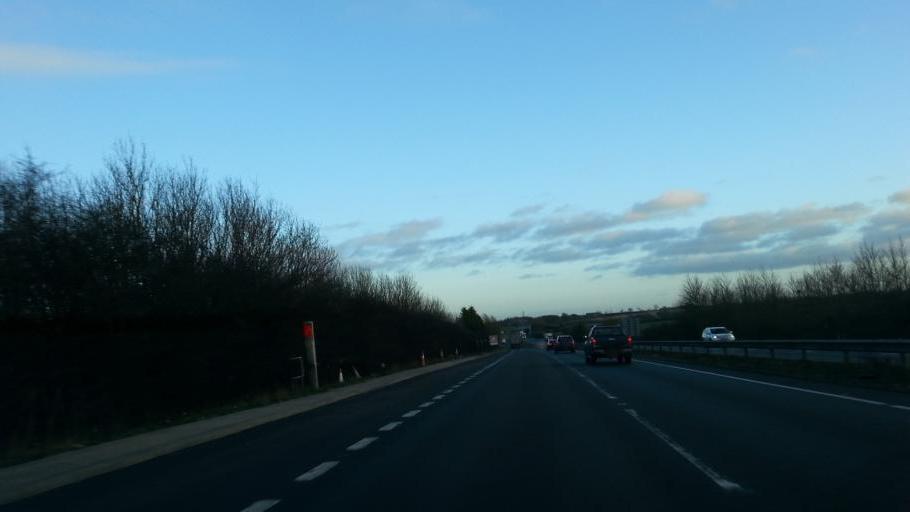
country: GB
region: England
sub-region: Northamptonshire
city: Thrapston
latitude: 52.3910
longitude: -0.5101
